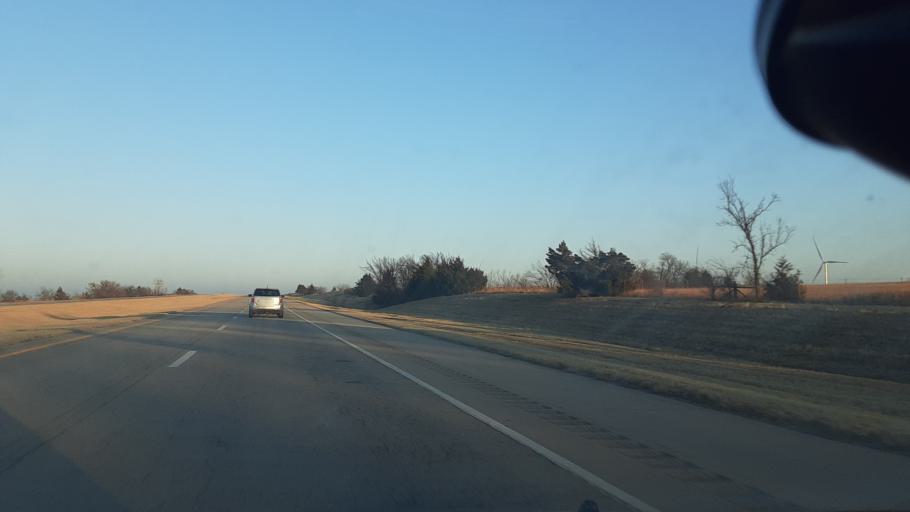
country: US
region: Oklahoma
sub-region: Noble County
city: Perry
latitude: 36.3977
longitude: -97.4430
